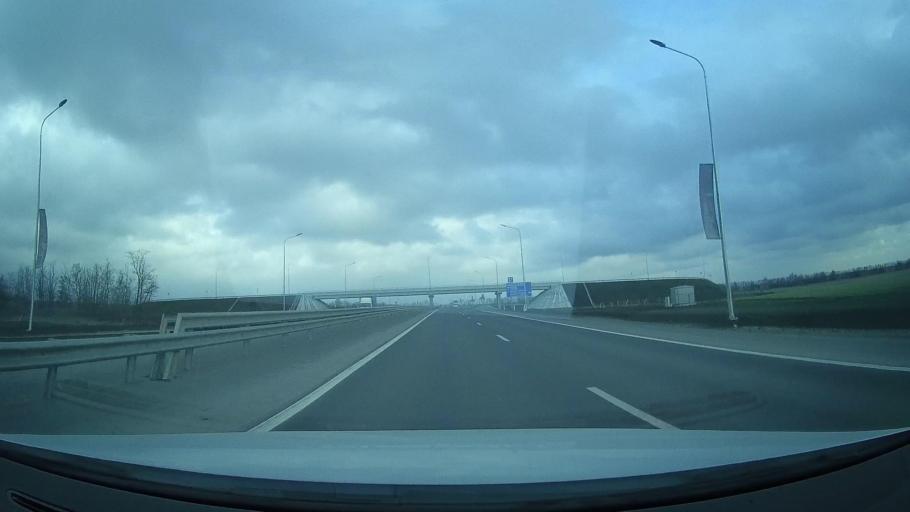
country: RU
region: Rostov
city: Grushevskaya
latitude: 47.4925
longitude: 39.9486
